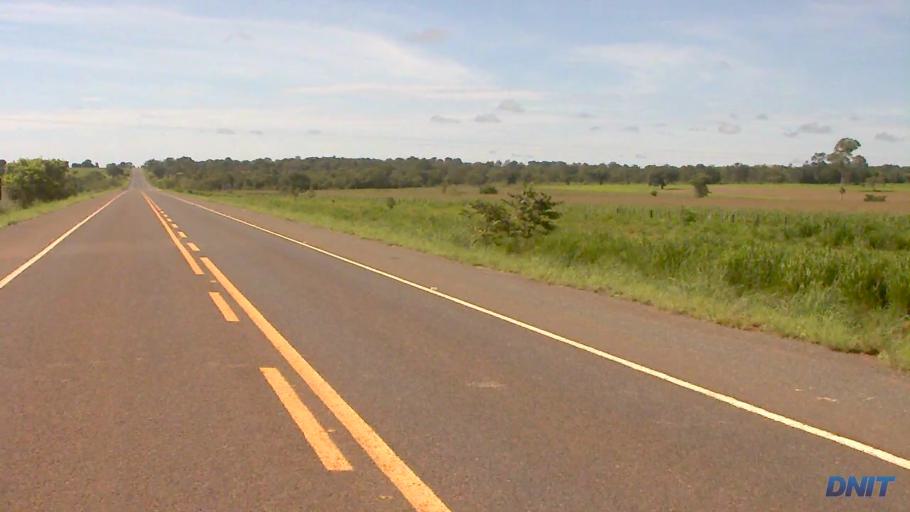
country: BR
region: Goias
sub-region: Sao Miguel Do Araguaia
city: Sao Miguel do Araguaia
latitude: -13.3895
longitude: -50.1383
